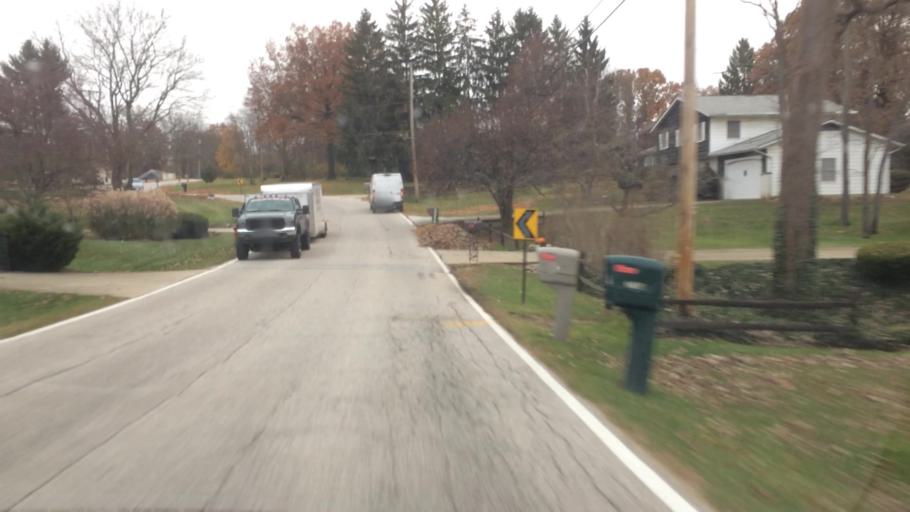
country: US
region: Ohio
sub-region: Summit County
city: Silver Lake
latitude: 41.1693
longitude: -81.4588
